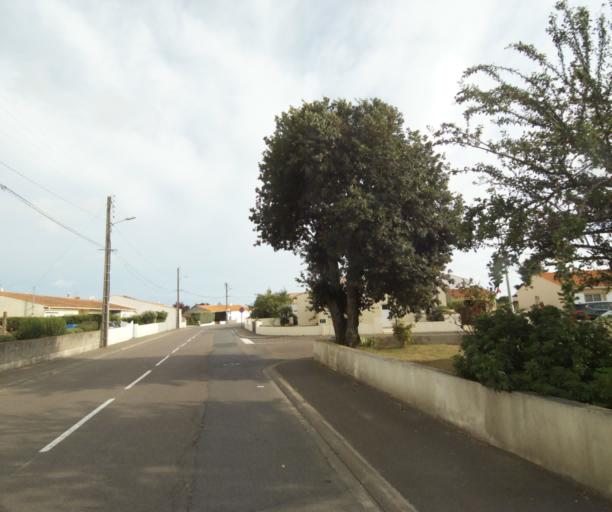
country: FR
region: Pays de la Loire
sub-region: Departement de la Vendee
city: Chateau-d'Olonne
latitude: 46.5018
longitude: -1.7334
